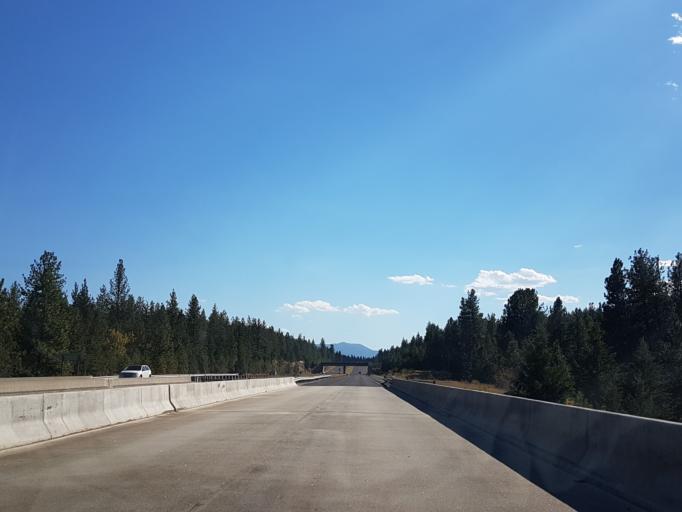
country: US
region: Montana
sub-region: Mineral County
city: Superior
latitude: 47.1307
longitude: -114.7967
